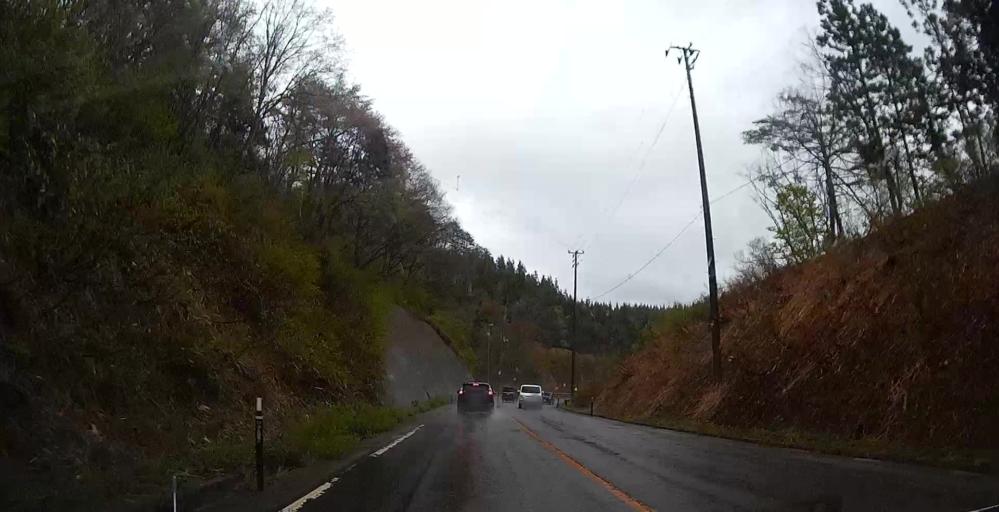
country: JP
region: Yamagata
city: Nagai
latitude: 38.0195
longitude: 139.8918
